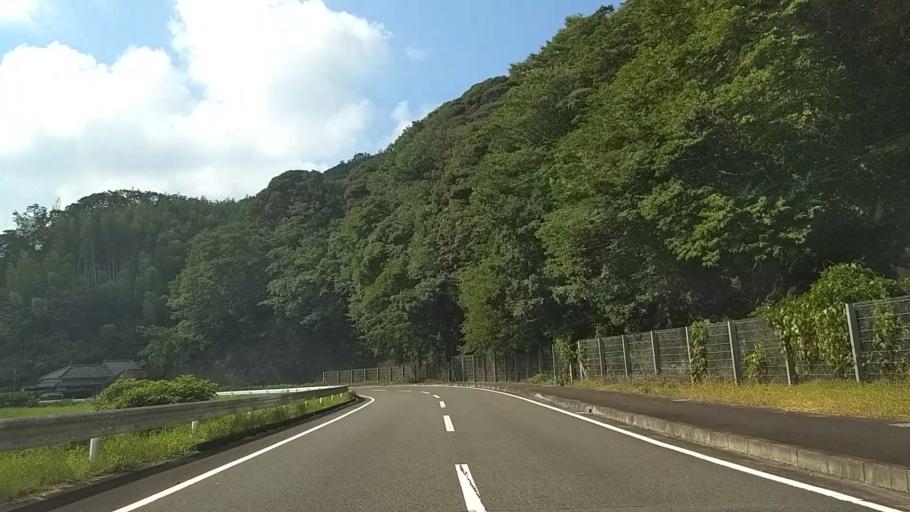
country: JP
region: Shizuoka
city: Shimoda
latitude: 34.6528
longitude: 138.8352
